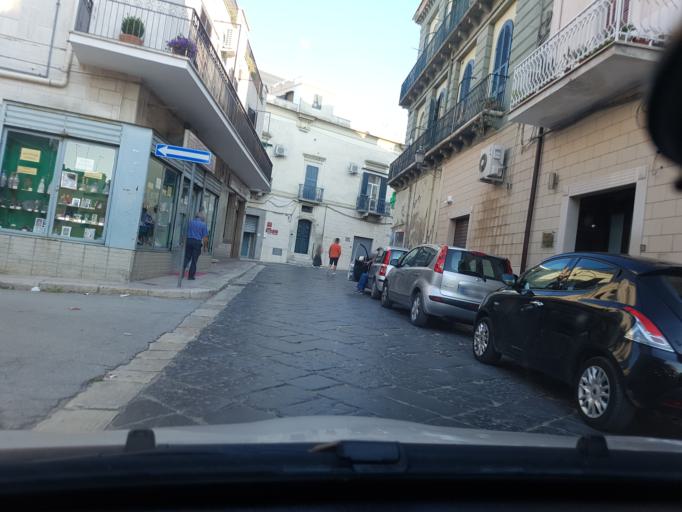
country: IT
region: Apulia
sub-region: Provincia di Foggia
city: Cerignola
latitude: 41.2675
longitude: 15.8946
